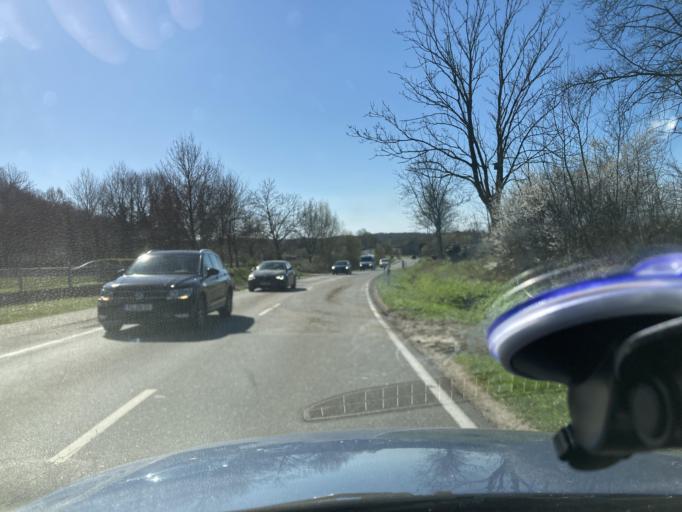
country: DE
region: Schleswig-Holstein
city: Nordhastedt
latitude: 54.1689
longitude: 9.1918
